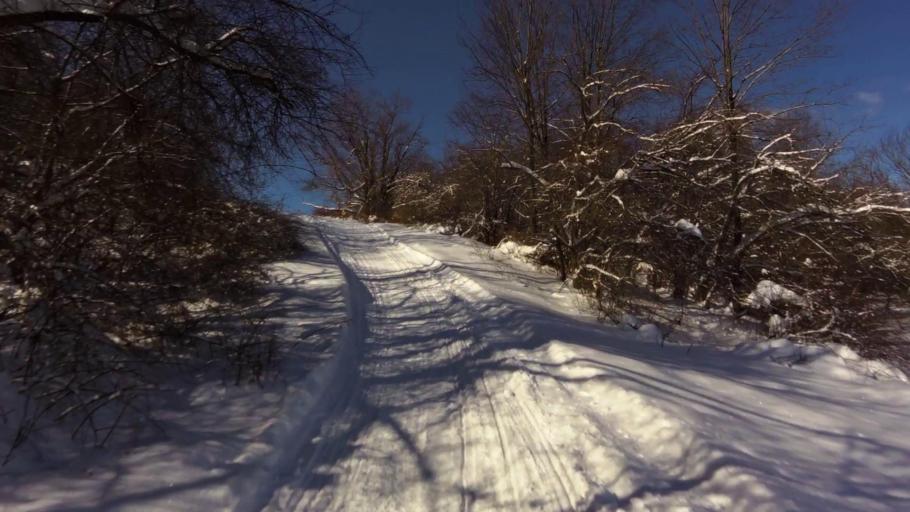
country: US
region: New York
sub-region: Chautauqua County
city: Fredonia
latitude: 42.3564
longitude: -79.1869
